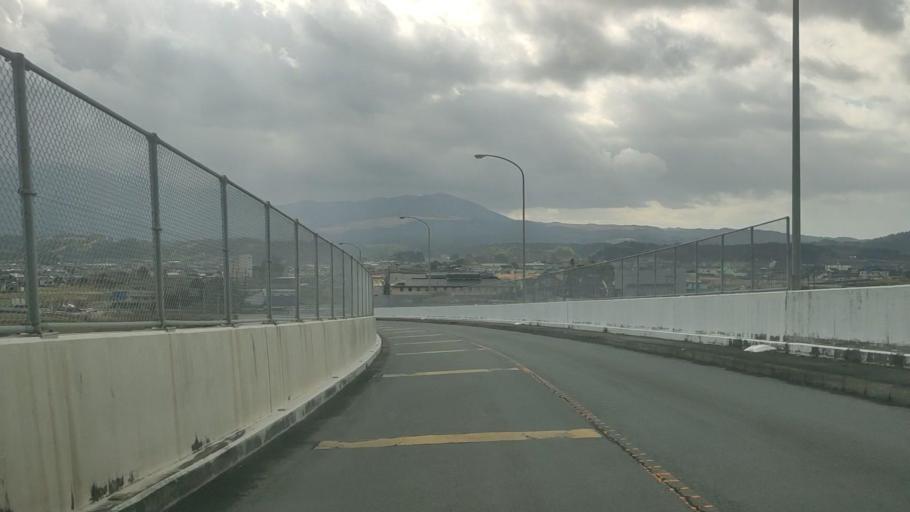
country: JP
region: Kumamoto
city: Hitoyoshi
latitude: 32.0552
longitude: 130.8171
